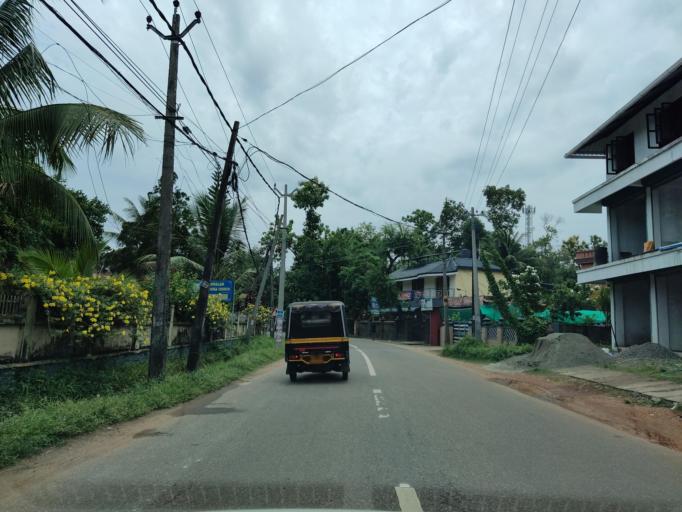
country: IN
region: Kerala
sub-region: Pattanamtitta
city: Adur
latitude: 9.2298
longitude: 76.6612
